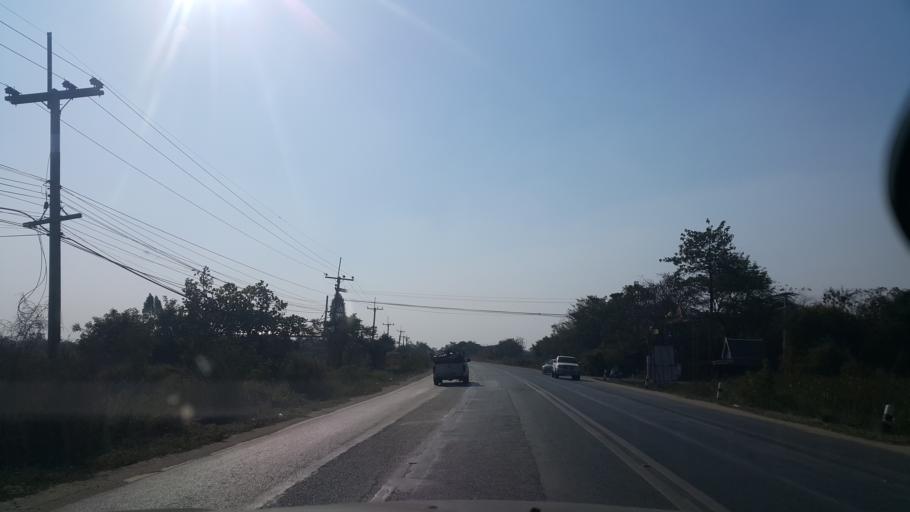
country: TH
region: Nakhon Ratchasima
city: Phimai
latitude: 15.2127
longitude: 102.4743
